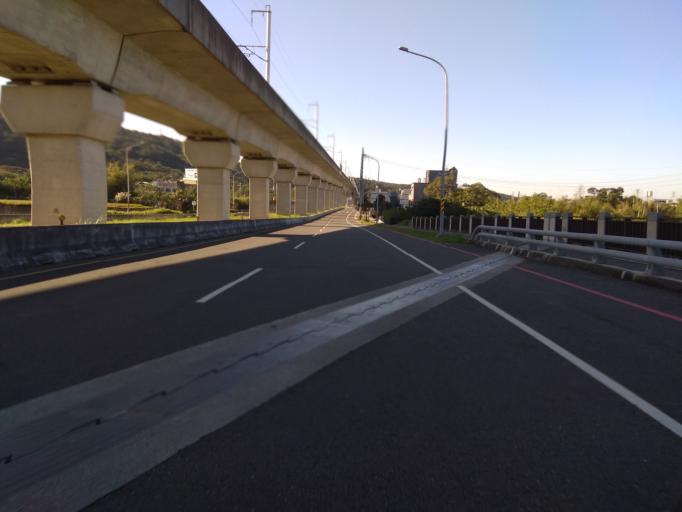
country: TW
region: Taiwan
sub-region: Hsinchu
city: Zhubei
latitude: 24.8841
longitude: 121.0707
